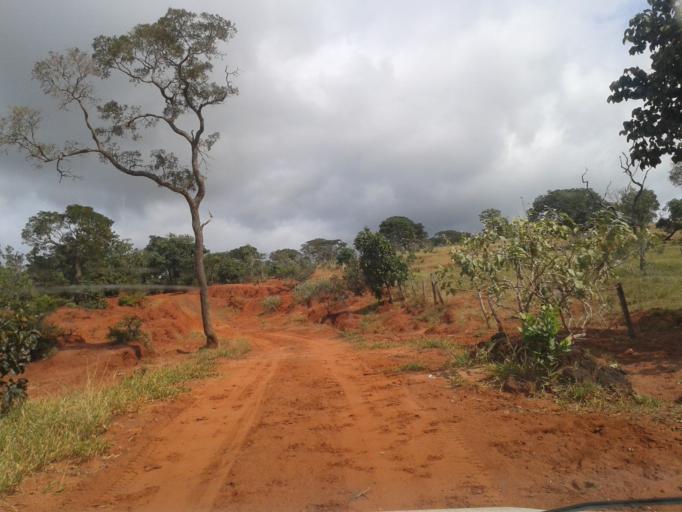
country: BR
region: Minas Gerais
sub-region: Campina Verde
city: Campina Verde
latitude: -19.4143
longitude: -49.6623
